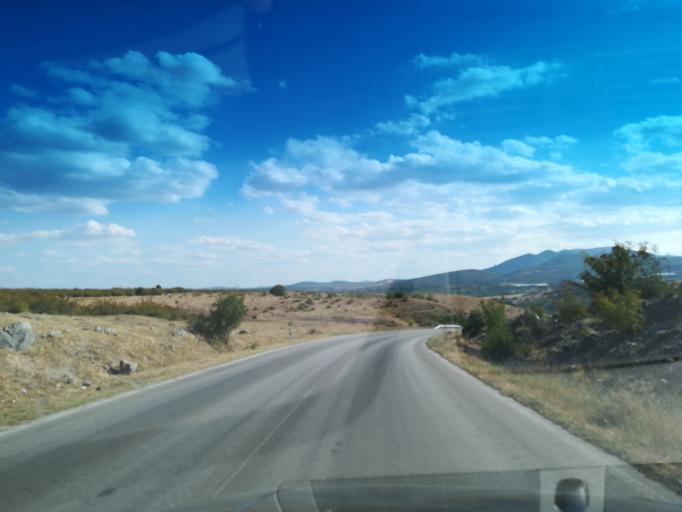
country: BG
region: Khaskovo
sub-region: Obshtina Mineralni Bani
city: Mineralni Bani
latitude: 41.9730
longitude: 25.3516
